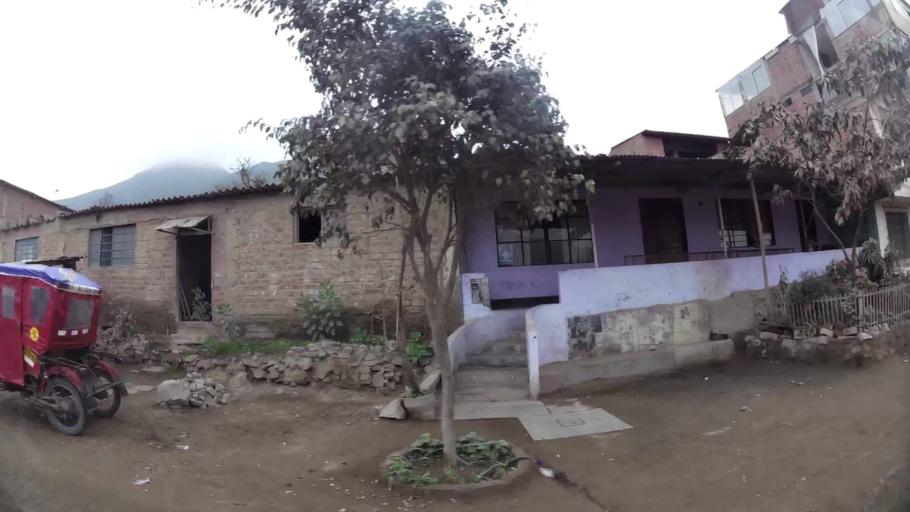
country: PE
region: Lima
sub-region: Lima
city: Cieneguilla
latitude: -12.2099
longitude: -76.9035
